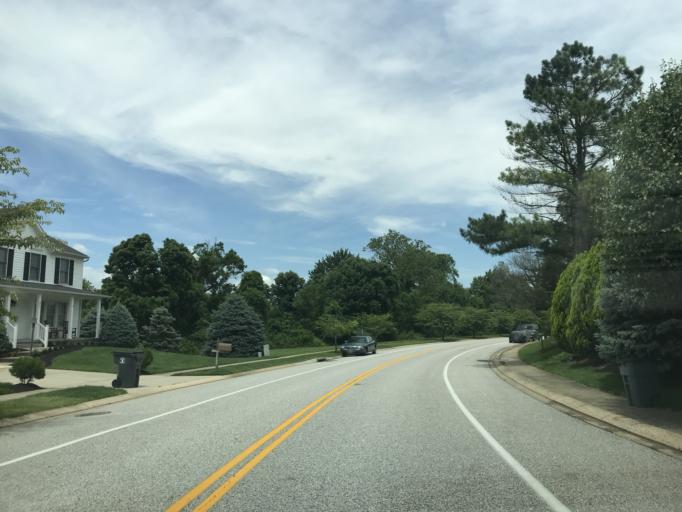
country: US
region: Maryland
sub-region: Harford County
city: South Bel Air
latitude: 39.5523
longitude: -76.3281
